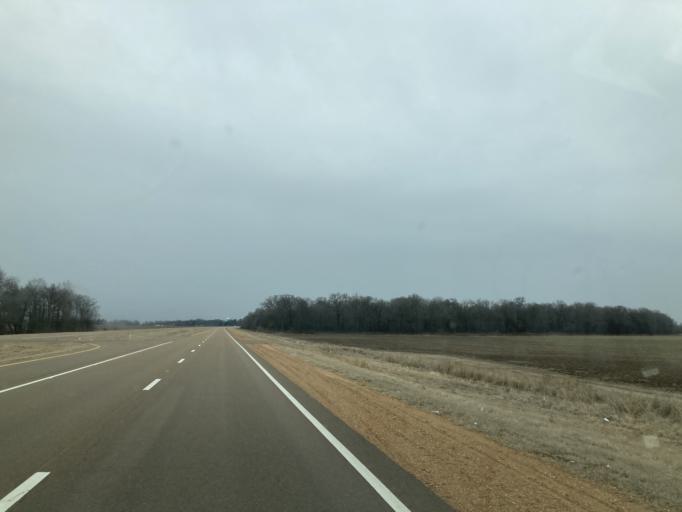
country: US
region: Mississippi
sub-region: Humphreys County
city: Belzoni
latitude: 33.0783
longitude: -90.4797
